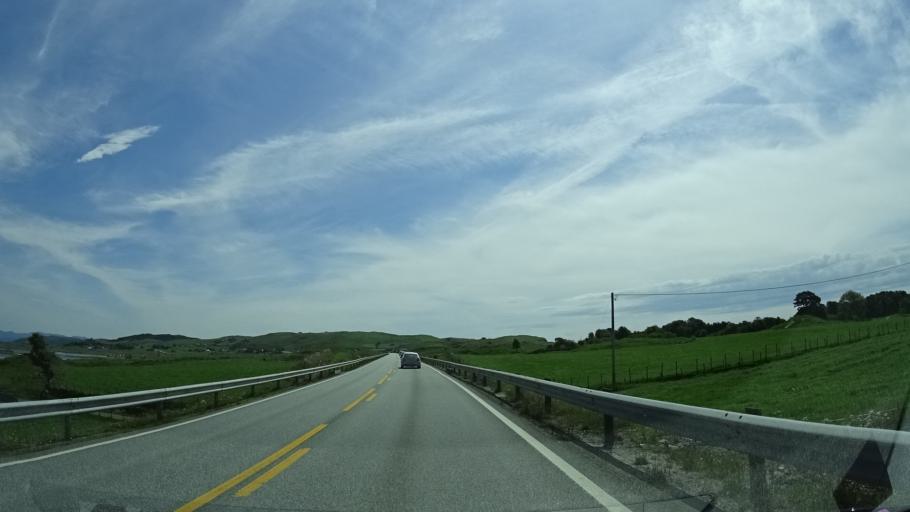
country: NO
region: Rogaland
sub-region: Rennesoy
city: Vikevag
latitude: 59.1339
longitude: 5.6055
